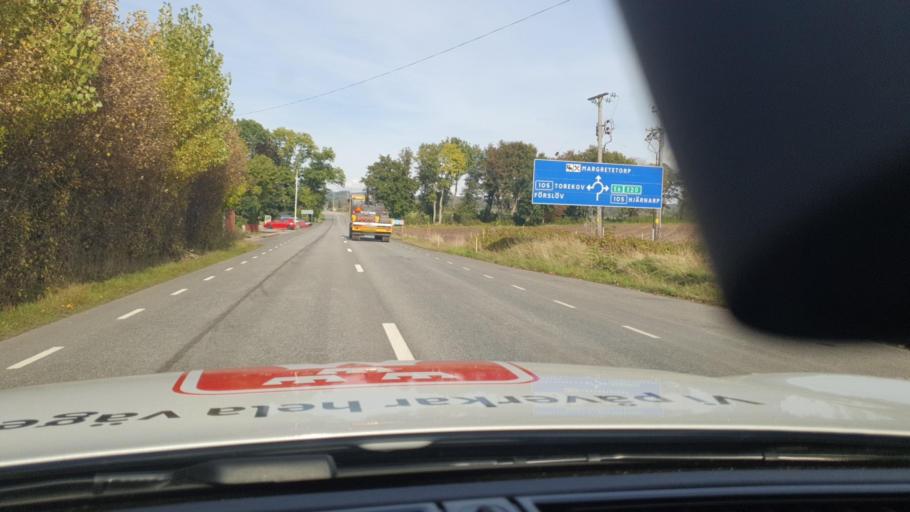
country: SE
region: Skane
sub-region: Angelholms Kommun
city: AEngelholm
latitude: 56.3162
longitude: 12.8870
